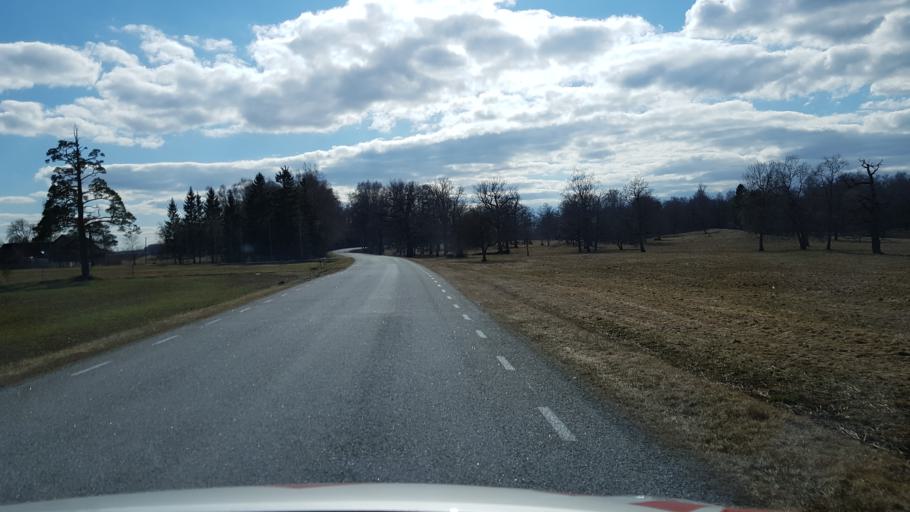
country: EE
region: Laeaene-Virumaa
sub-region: Rakvere linn
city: Rakvere
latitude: 59.3245
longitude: 26.2707
